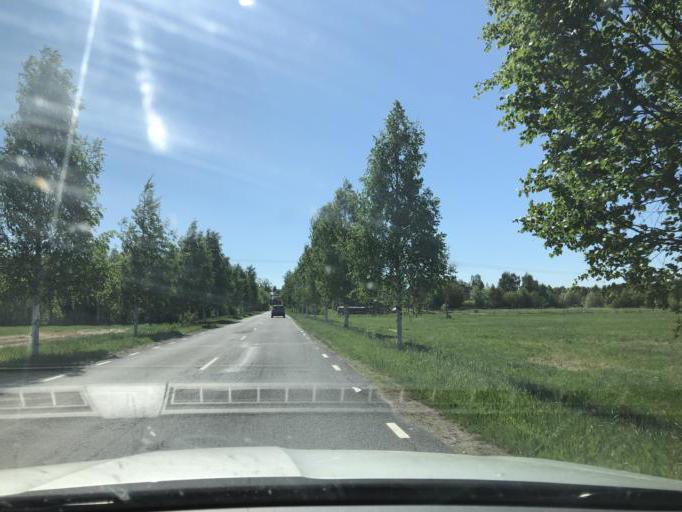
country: SE
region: Norrbotten
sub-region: Lulea Kommun
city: Gammelstad
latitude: 65.6498
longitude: 22.0199
